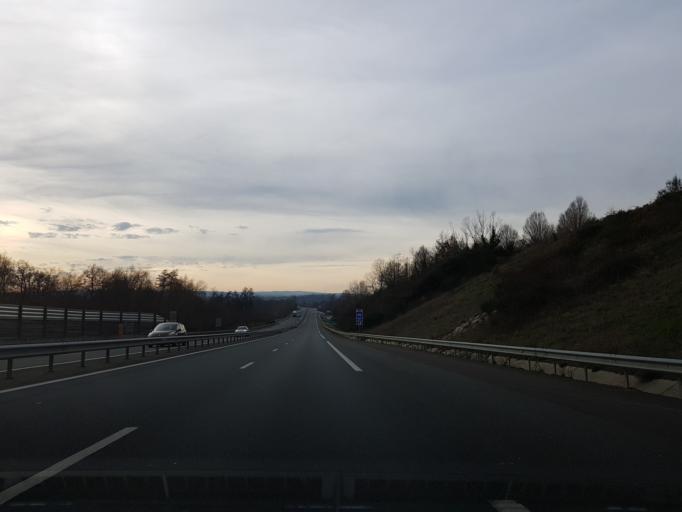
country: FR
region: Auvergne
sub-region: Departement de l'Allier
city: Saint-Victor
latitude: 46.3797
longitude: 2.6115
